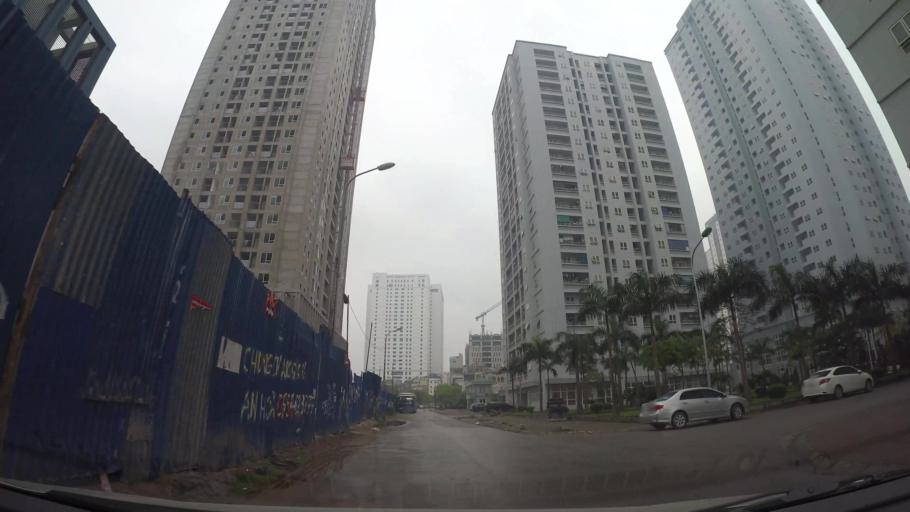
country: VN
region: Ha Noi
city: Cau Giay
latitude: 21.0181
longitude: 105.7883
